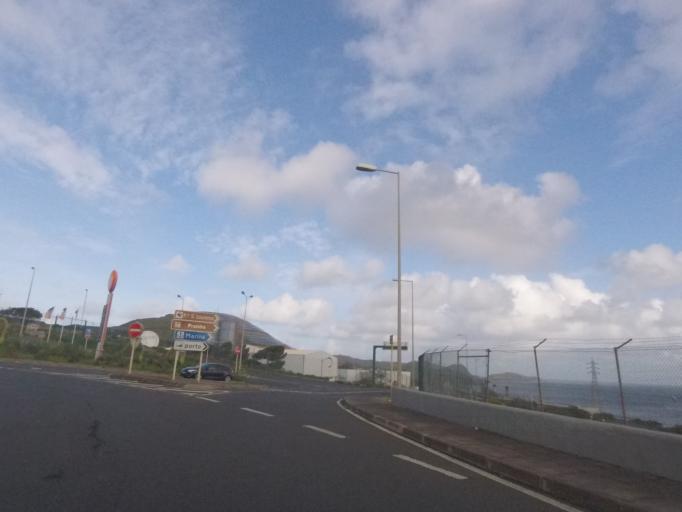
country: PT
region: Madeira
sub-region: Machico
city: Canical
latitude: 32.7422
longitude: -16.7362
